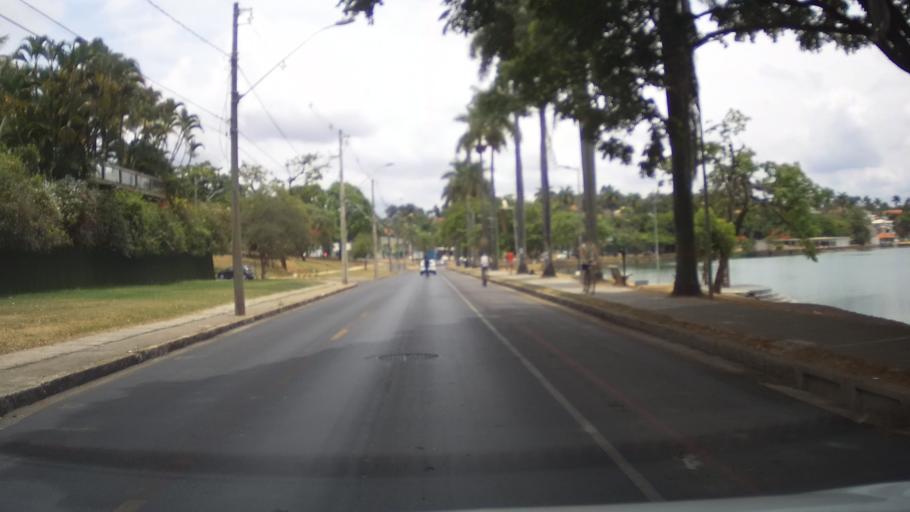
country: BR
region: Minas Gerais
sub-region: Belo Horizonte
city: Belo Horizonte
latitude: -19.8523
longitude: -43.9680
